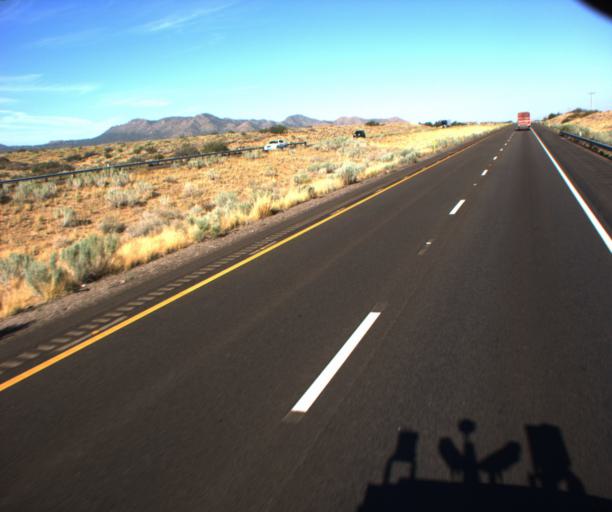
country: US
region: Arizona
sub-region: Mohave County
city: New Kingman-Butler
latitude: 35.1947
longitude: -113.8428
